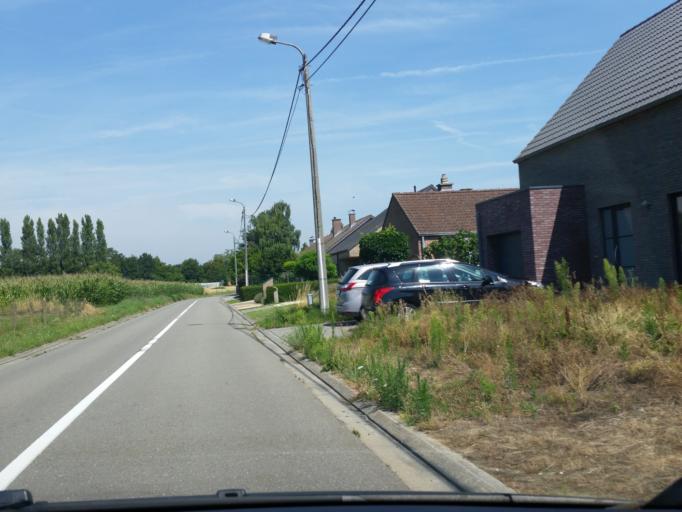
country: BE
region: Flanders
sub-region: Provincie Vlaams-Brabant
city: Zemst
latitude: 50.9756
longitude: 4.4545
